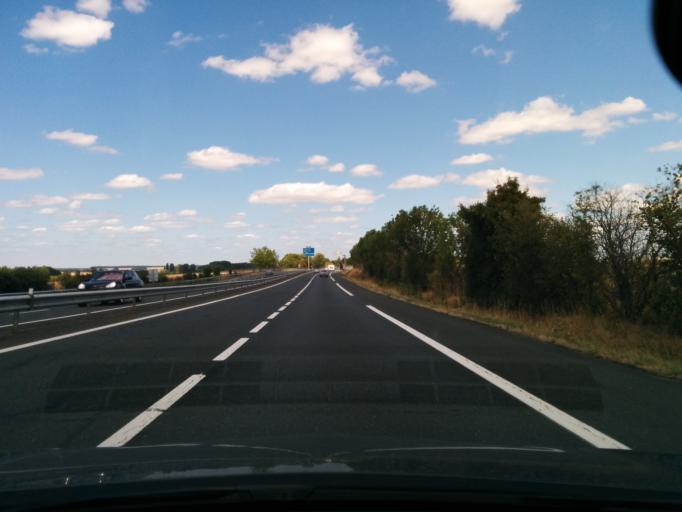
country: FR
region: Centre
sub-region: Departement de l'Indre
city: Vatan
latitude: 47.0428
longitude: 1.7960
